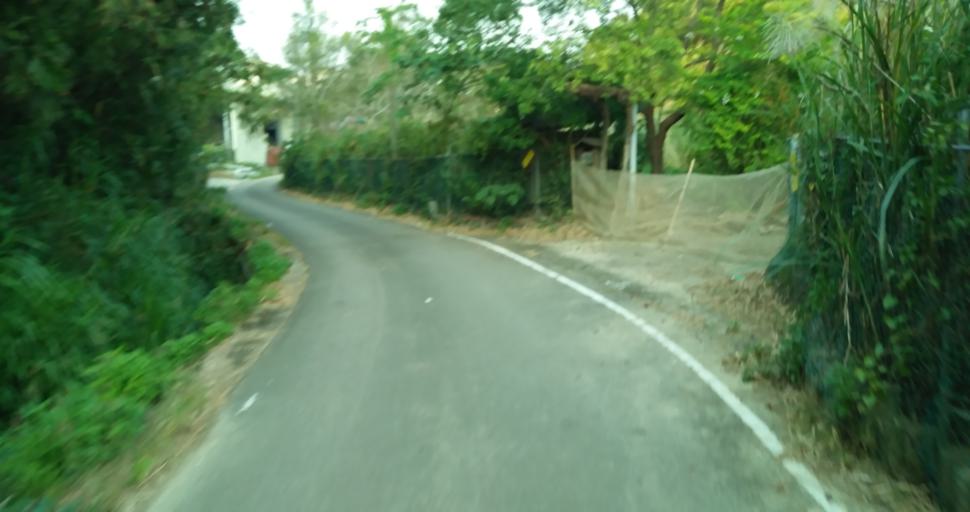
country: TW
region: Taiwan
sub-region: Hsinchu
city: Hsinchu
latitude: 24.7621
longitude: 120.9640
